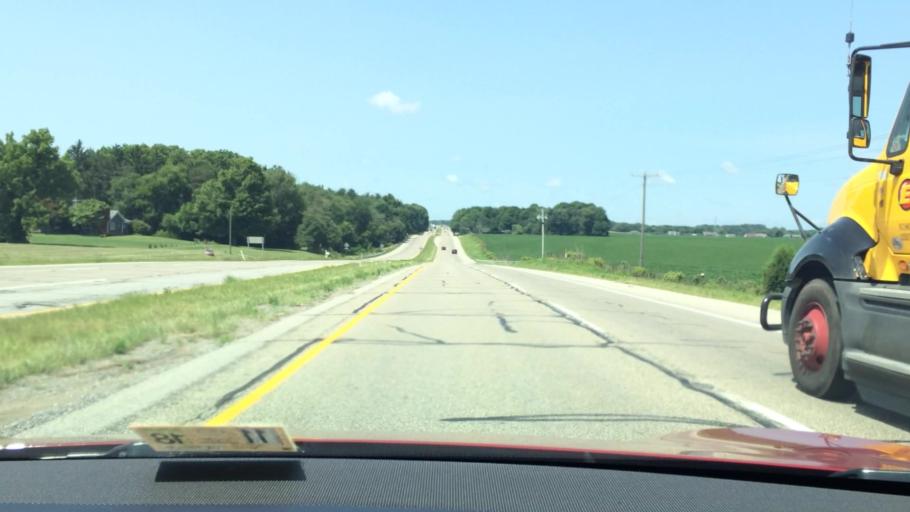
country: US
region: Indiana
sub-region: LaPorte County
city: Hudson Lake
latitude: 41.6728
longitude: -86.5660
